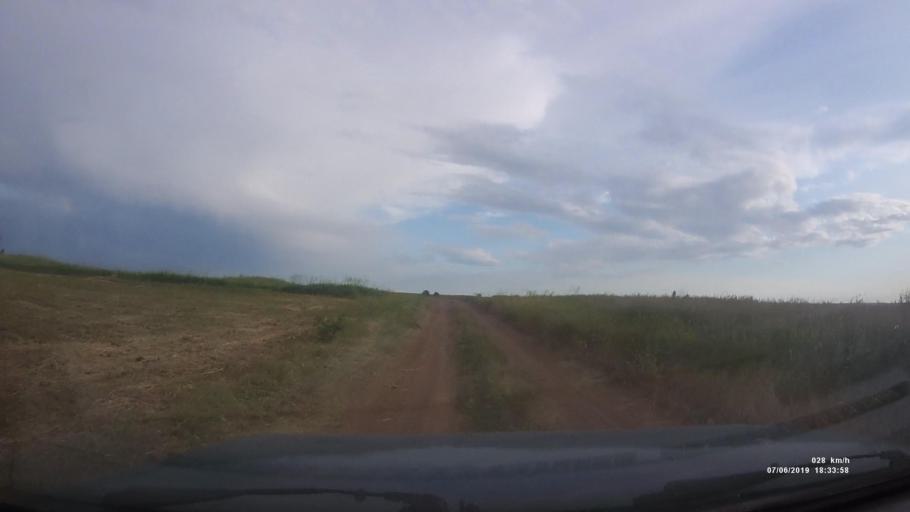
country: RU
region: Rostov
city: Staraya Stanitsa
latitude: 48.2598
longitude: 40.3621
